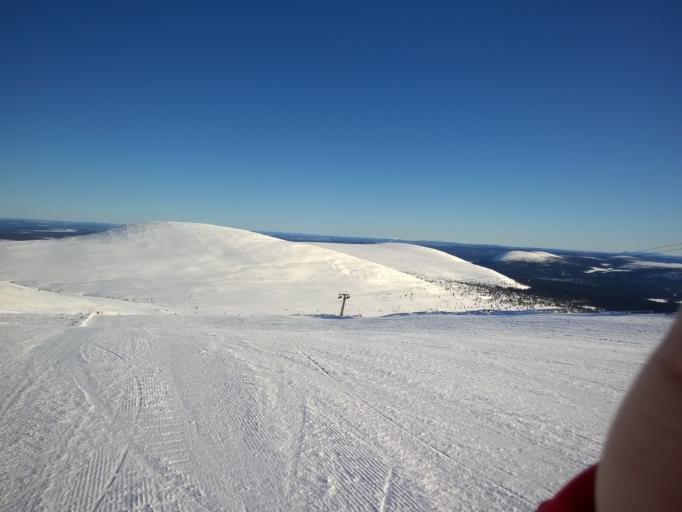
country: FI
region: Lapland
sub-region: Tunturi-Lappi
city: Muonio
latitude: 68.0614
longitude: 24.0395
